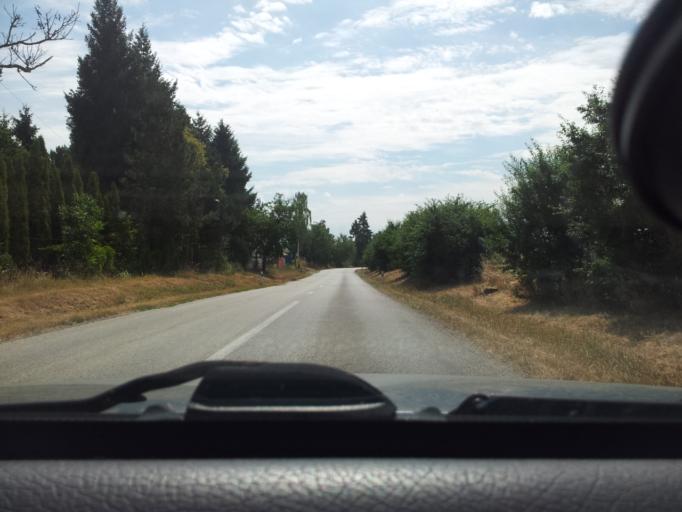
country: SK
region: Nitriansky
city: Zlate Moravce
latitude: 48.3769
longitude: 18.4110
